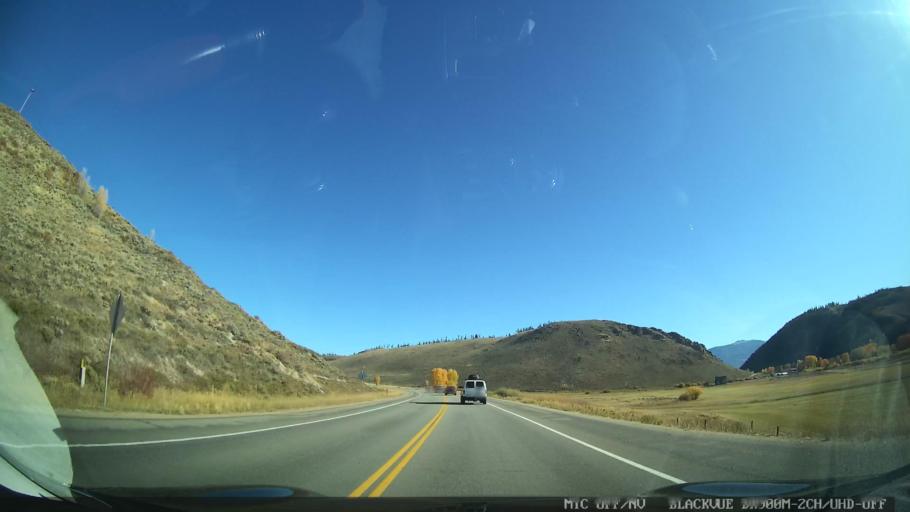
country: US
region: Colorado
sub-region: Grand County
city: Granby
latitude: 40.1243
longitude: -105.8996
